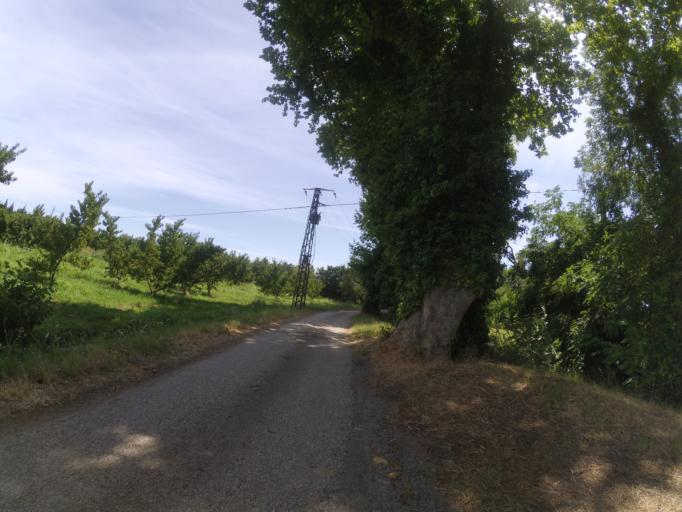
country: FR
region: Languedoc-Roussillon
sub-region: Departement des Pyrenees-Orientales
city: Ille-sur-Tet
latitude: 42.6755
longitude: 2.6510
